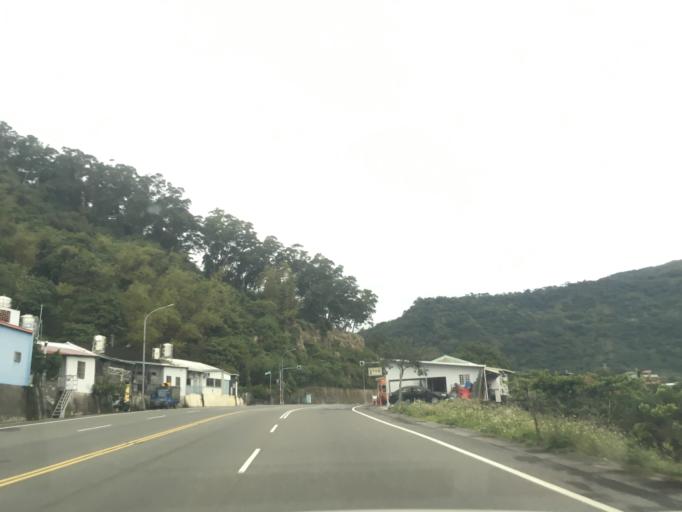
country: TW
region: Taiwan
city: Taitung City
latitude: 22.7592
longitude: 121.0503
